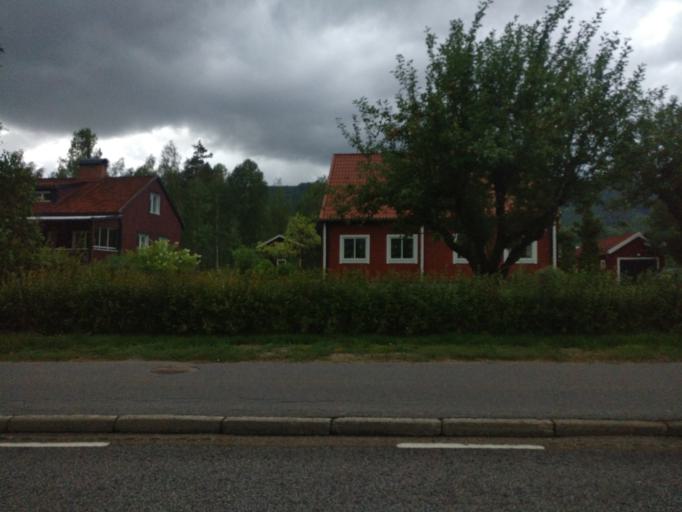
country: SE
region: Vaermland
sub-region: Torsby Kommun
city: Torsby
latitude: 60.7258
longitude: 12.8766
